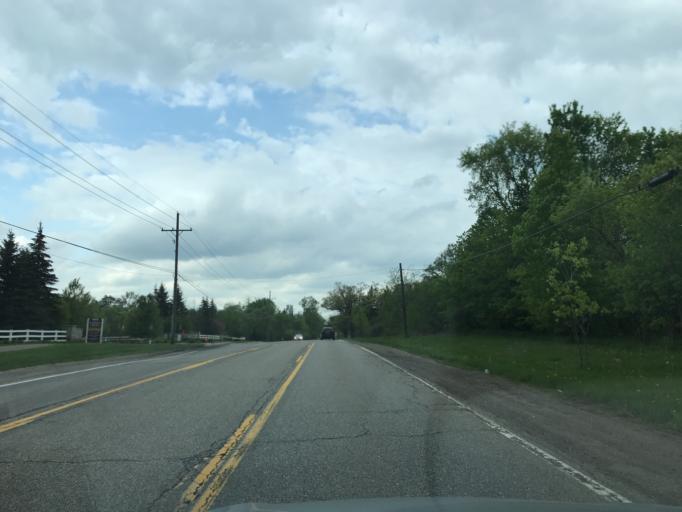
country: US
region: Michigan
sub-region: Oakland County
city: South Lyon
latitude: 42.4852
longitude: -83.6529
